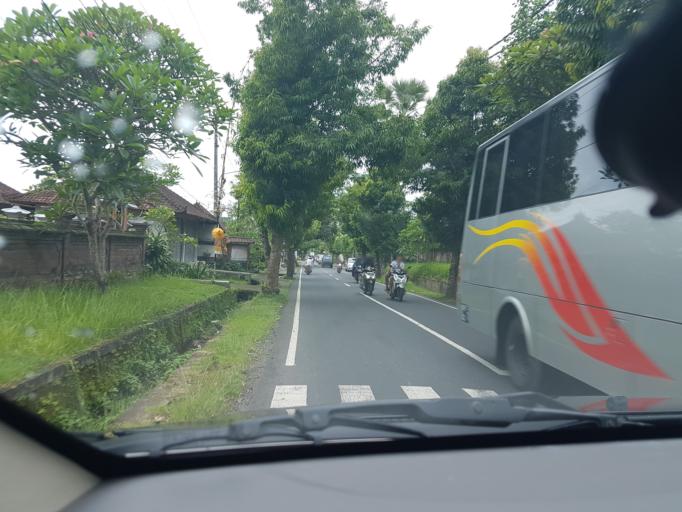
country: ID
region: Bali
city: Banjar Pande
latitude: -8.5092
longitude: 115.2416
